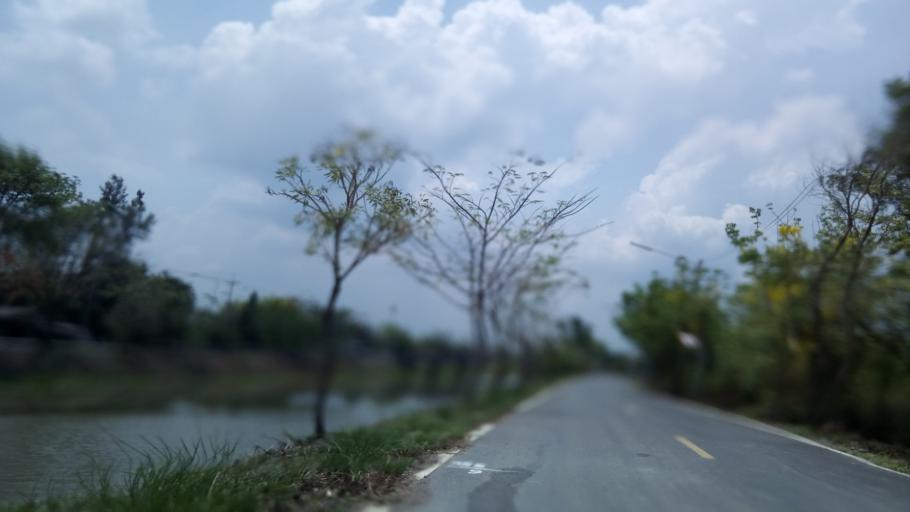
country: TH
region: Pathum Thani
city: Nong Suea
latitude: 14.1102
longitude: 100.8236
